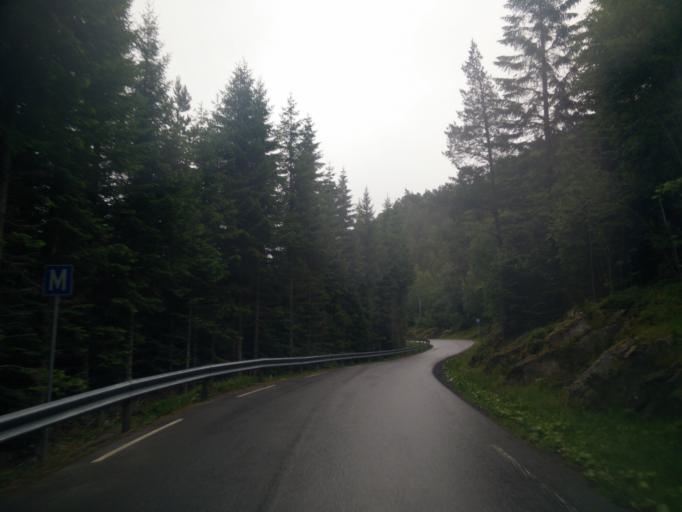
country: NO
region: More og Romsdal
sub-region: Kristiansund
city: Rensvik
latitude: 63.0311
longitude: 7.9111
